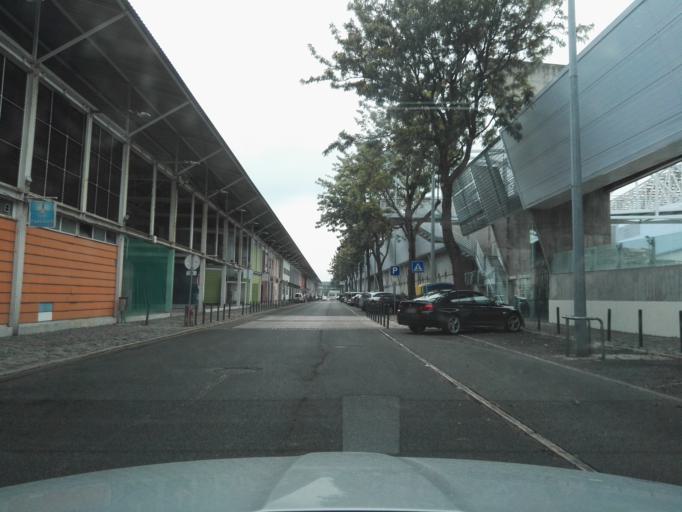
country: PT
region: Lisbon
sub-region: Loures
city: Moscavide
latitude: 38.7729
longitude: -9.0925
